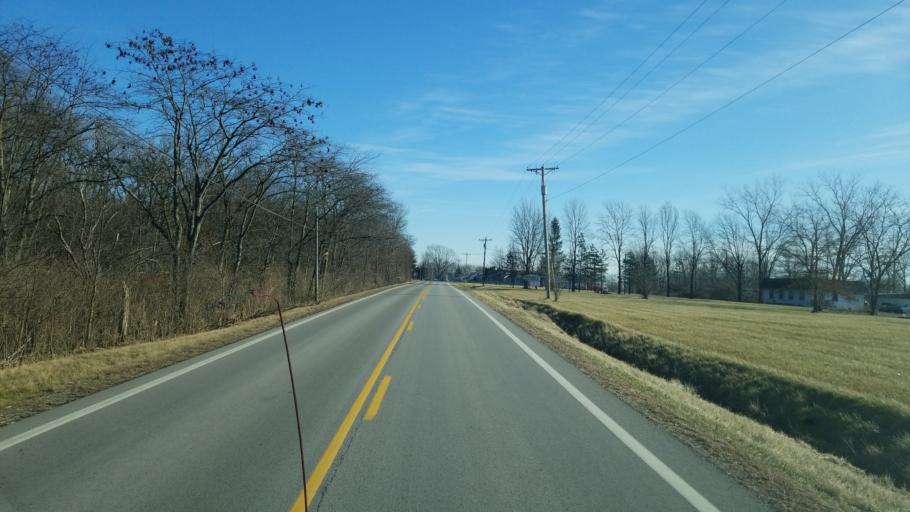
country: US
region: Ohio
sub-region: Wood County
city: Weston
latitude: 41.4104
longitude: -83.8863
